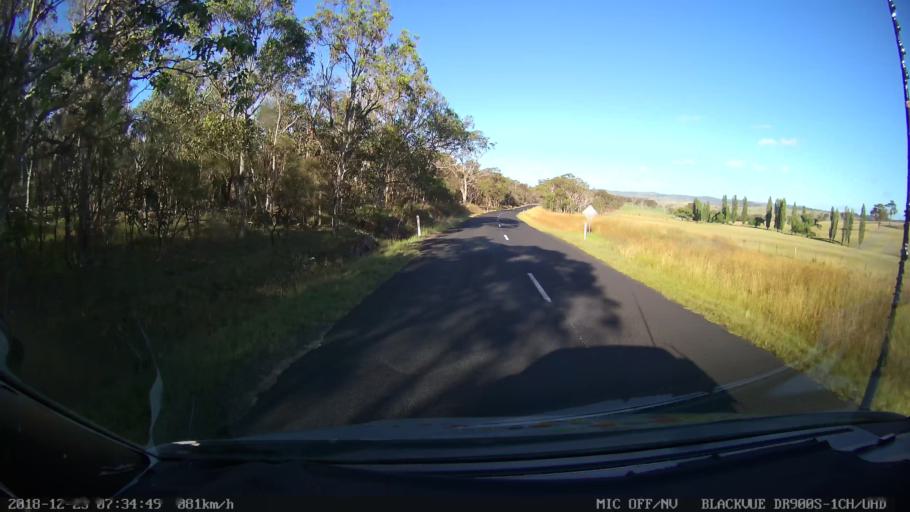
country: AU
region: New South Wales
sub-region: Armidale Dumaresq
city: Enmore
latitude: -30.5219
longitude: 152.0889
